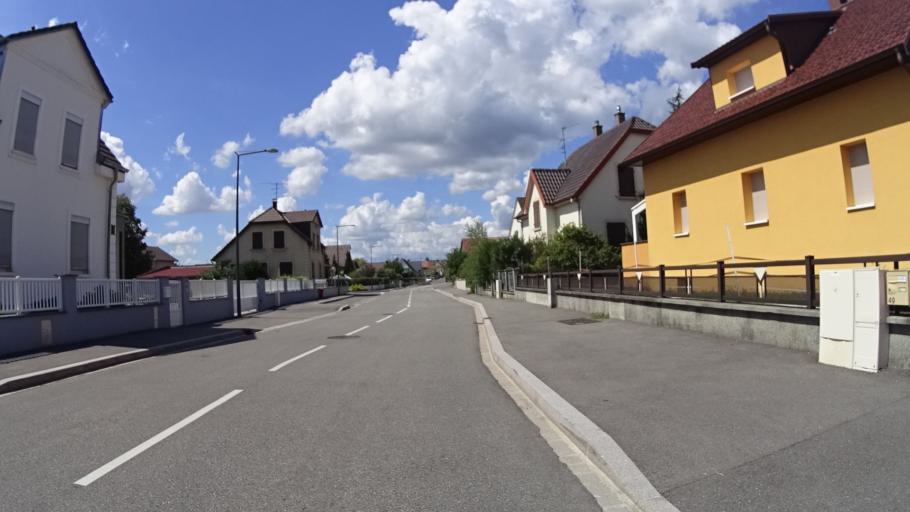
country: FR
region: Alsace
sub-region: Departement du Haut-Rhin
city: Bantzenheim
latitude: 47.8233
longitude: 7.5207
